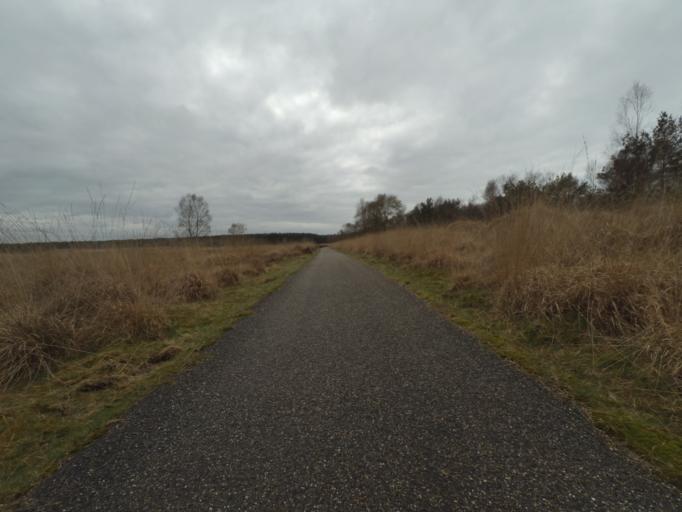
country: NL
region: Gelderland
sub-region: Gemeente Rozendaal
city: Rozendaal
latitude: 52.0347
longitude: 5.9386
